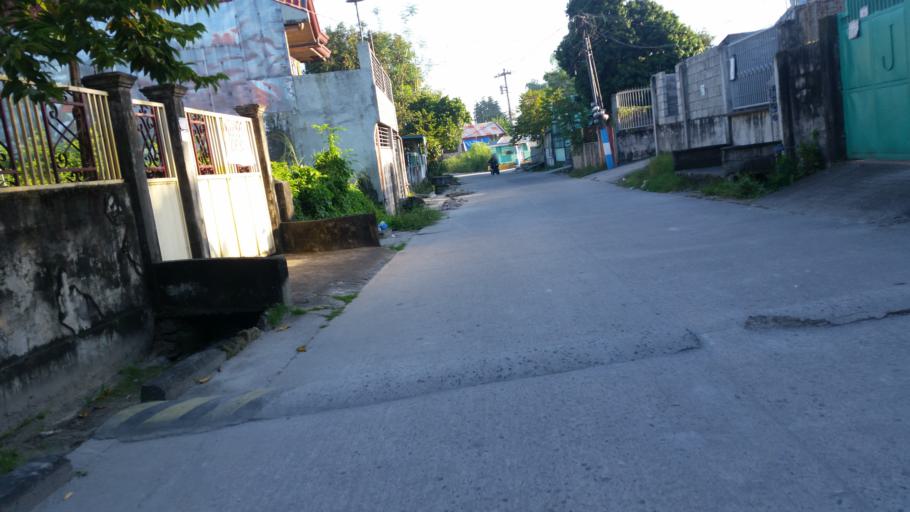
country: PH
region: Central Luzon
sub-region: Province of Pampanga
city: Mabalacat City
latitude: 15.2758
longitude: 120.5698
